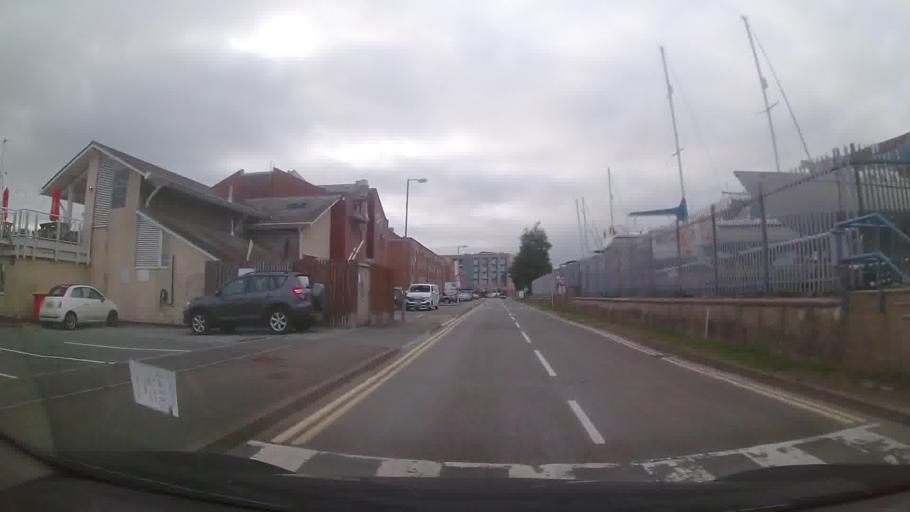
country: GB
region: Wales
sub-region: Pembrokeshire
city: Milford Haven
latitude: 51.7119
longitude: -5.0373
